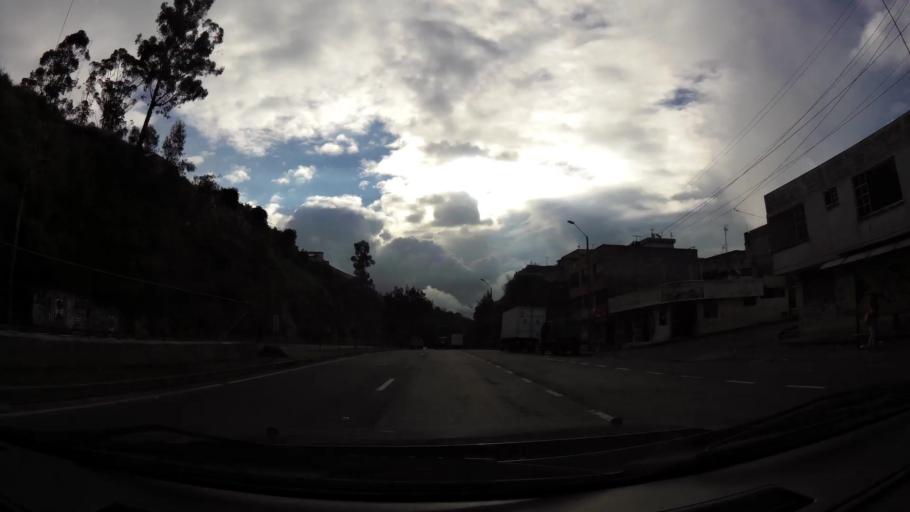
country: EC
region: Pichincha
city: Quito
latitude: -0.2343
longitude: -78.4915
